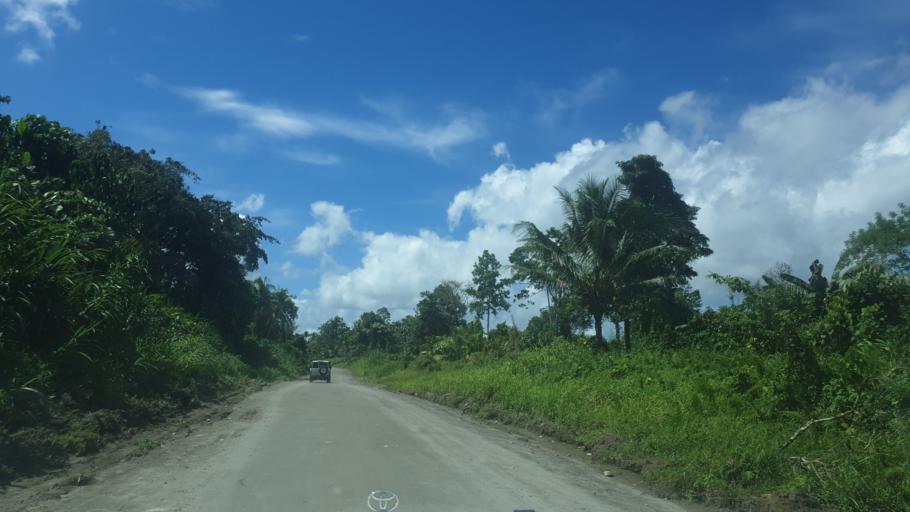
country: PG
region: Bougainville
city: Panguna
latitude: -6.6614
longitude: 155.4525
